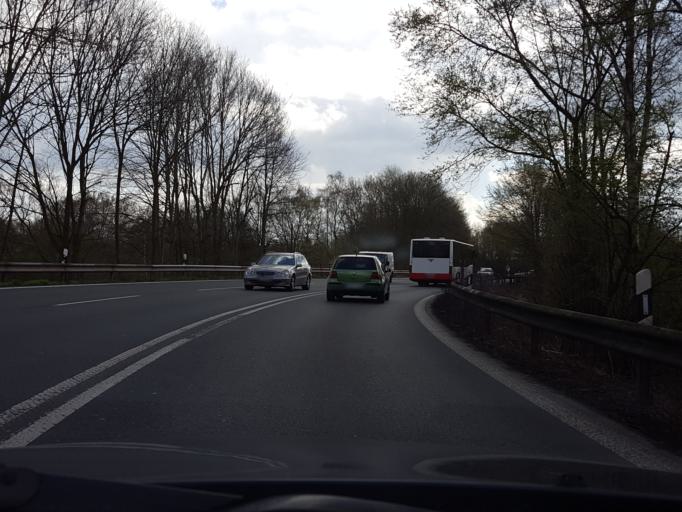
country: DE
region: North Rhine-Westphalia
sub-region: Regierungsbezirk Munster
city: Recklinghausen
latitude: 51.5882
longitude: 7.2144
